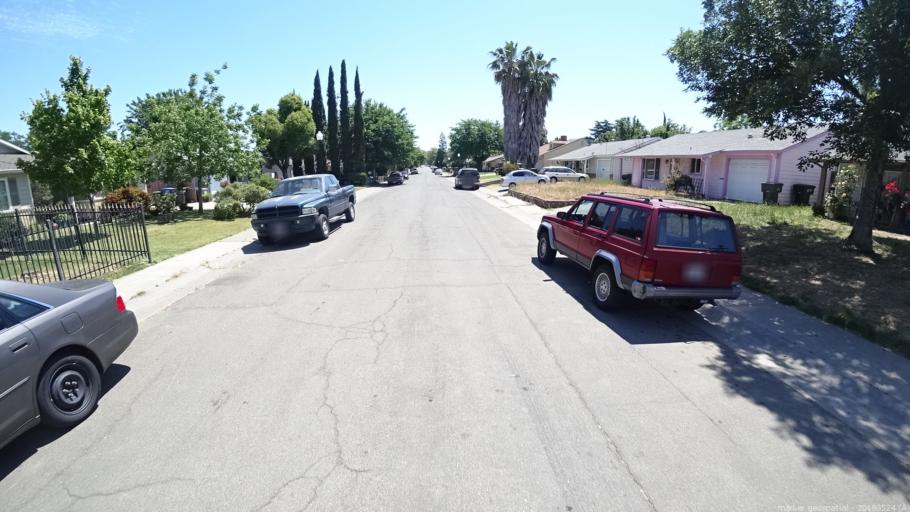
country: US
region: California
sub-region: Sacramento County
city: Sacramento
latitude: 38.6121
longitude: -121.4656
